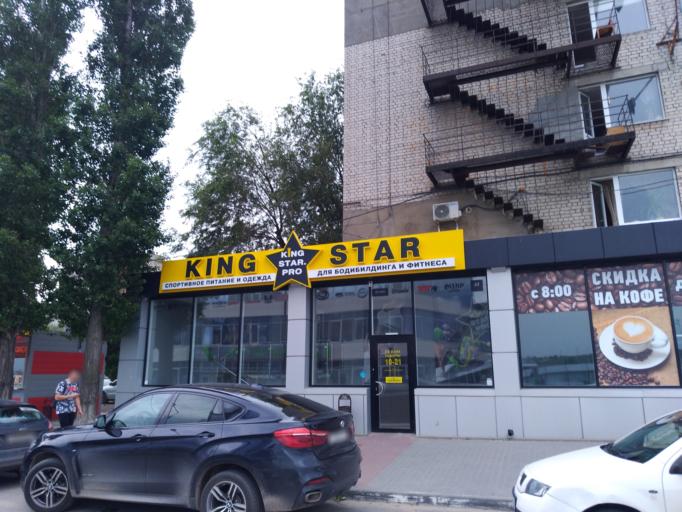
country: RU
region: Volgograd
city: Volgograd
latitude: 48.7297
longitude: 44.5241
